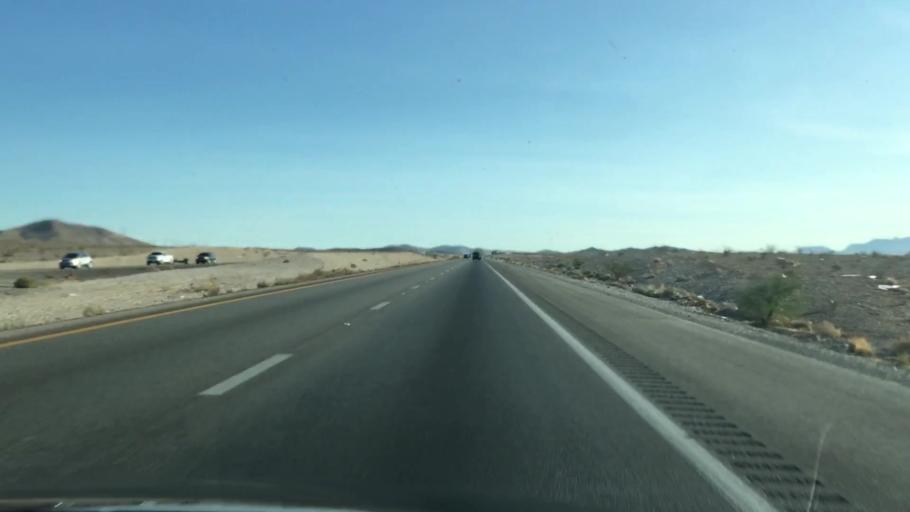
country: US
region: Nevada
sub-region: Clark County
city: Nellis Air Force Base
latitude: 36.3003
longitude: -114.9784
